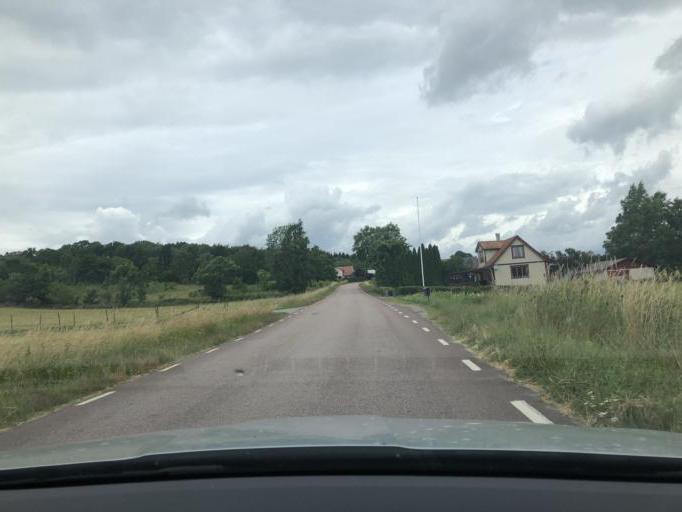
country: SE
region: Blekinge
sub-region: Solvesborgs Kommun
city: Soelvesborg
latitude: 56.1320
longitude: 14.6077
